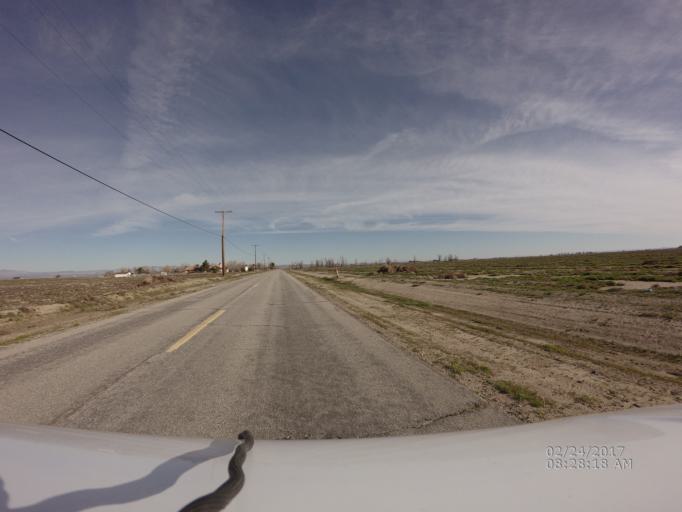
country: US
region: California
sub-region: Los Angeles County
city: Lancaster
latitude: 34.7353
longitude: -118.0232
